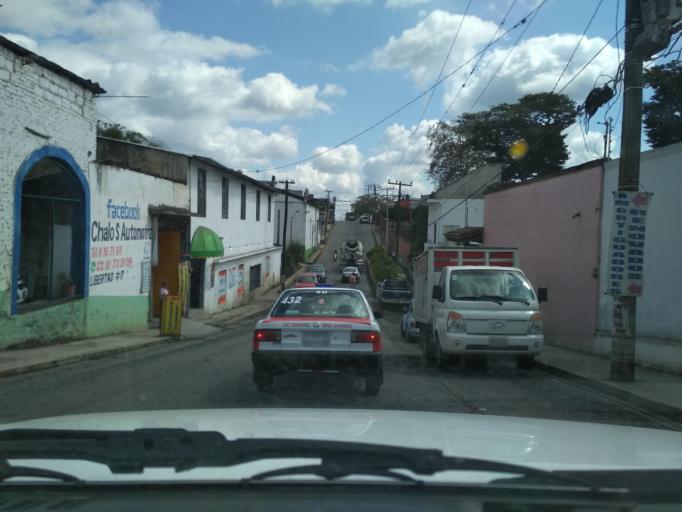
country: MX
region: Veracruz
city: Coatepec
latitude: 19.4519
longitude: -96.9521
